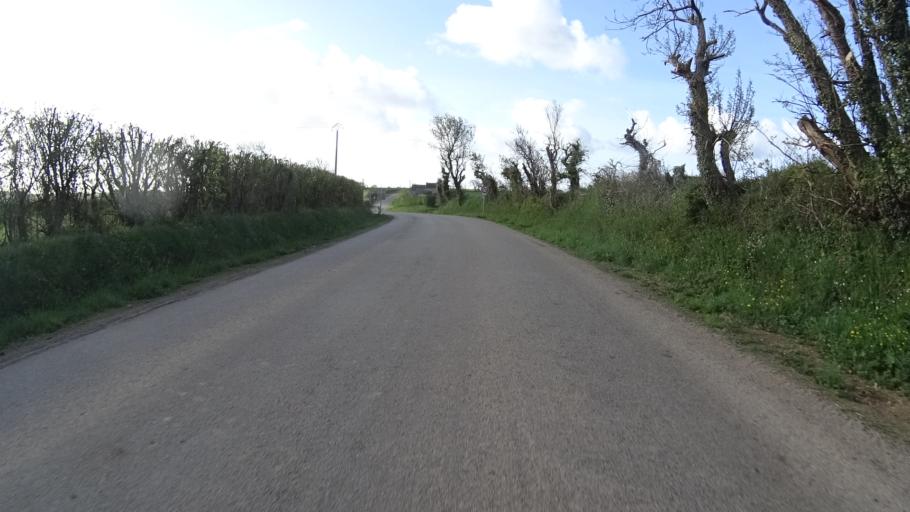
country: FR
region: Brittany
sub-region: Departement du Finistere
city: Plouzane
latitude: 48.3939
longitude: -4.6644
